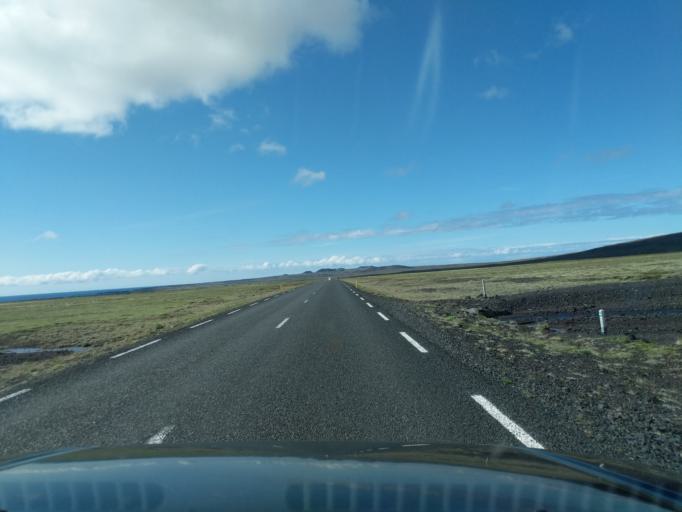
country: IS
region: West
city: Olafsvik
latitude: 64.7942
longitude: -23.9178
